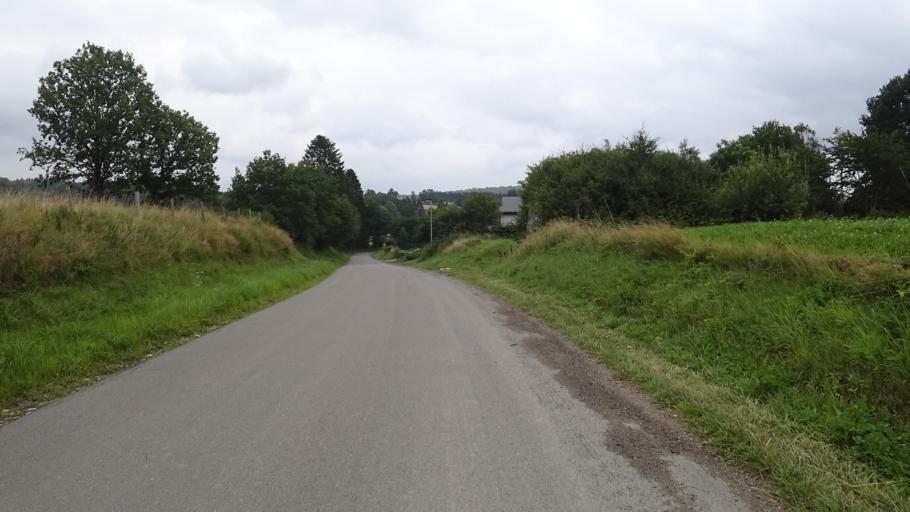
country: BE
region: Wallonia
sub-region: Province du Luxembourg
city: Chiny
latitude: 49.7995
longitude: 5.3763
